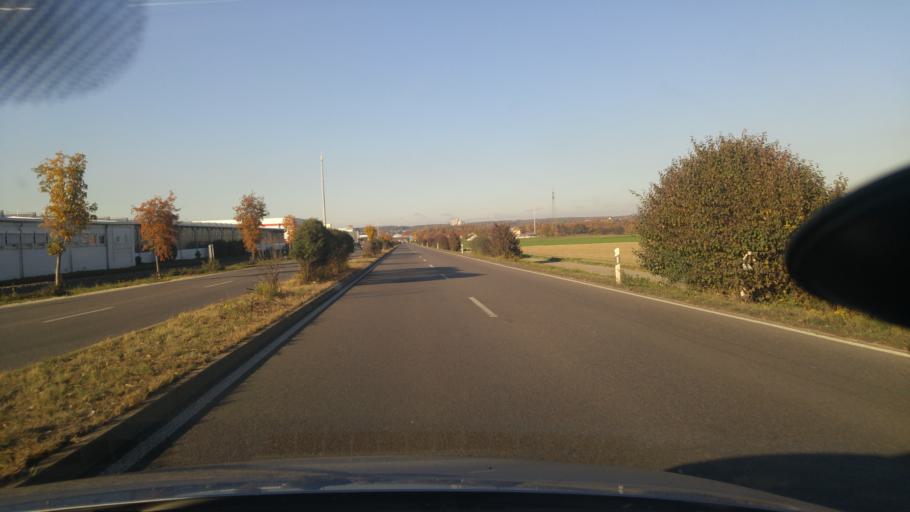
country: DE
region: Baden-Wuerttemberg
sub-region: Regierungsbezirk Stuttgart
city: Dettingen unter Teck
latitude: 48.6217
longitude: 9.4554
